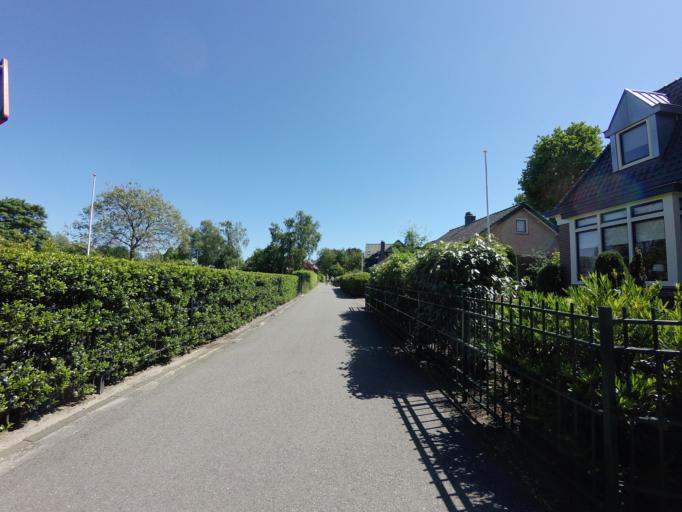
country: NL
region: Utrecht
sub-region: Gemeente Soest
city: Soest
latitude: 52.1836
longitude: 5.3030
